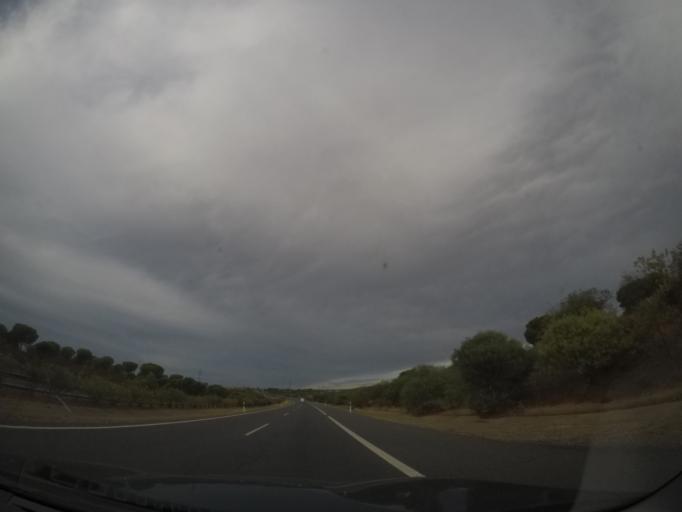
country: ES
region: Andalusia
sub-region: Provincia de Huelva
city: Cartaya
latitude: 37.3121
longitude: -7.1944
